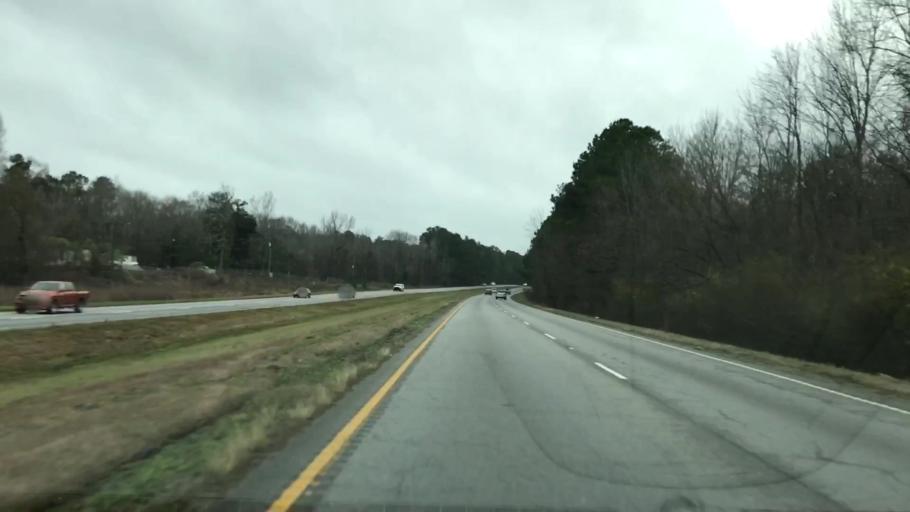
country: US
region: South Carolina
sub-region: Berkeley County
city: Goose Creek
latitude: 33.0479
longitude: -80.0335
